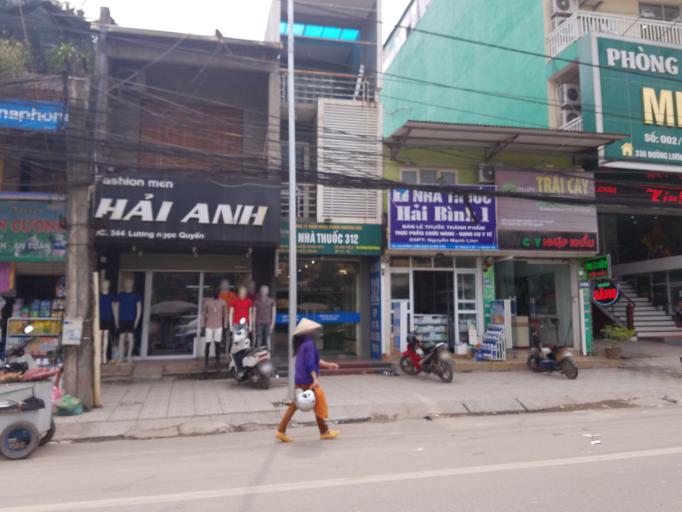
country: VN
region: Thai Nguyen
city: Thanh Pho Thai Nguyen
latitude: 21.5873
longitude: 105.8301
